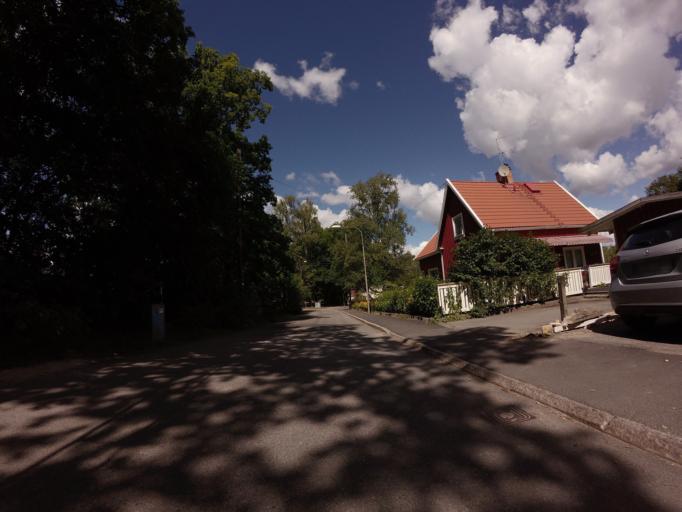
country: SE
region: Stockholm
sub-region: Huddinge Kommun
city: Segeltorp
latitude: 59.3006
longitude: 17.9709
